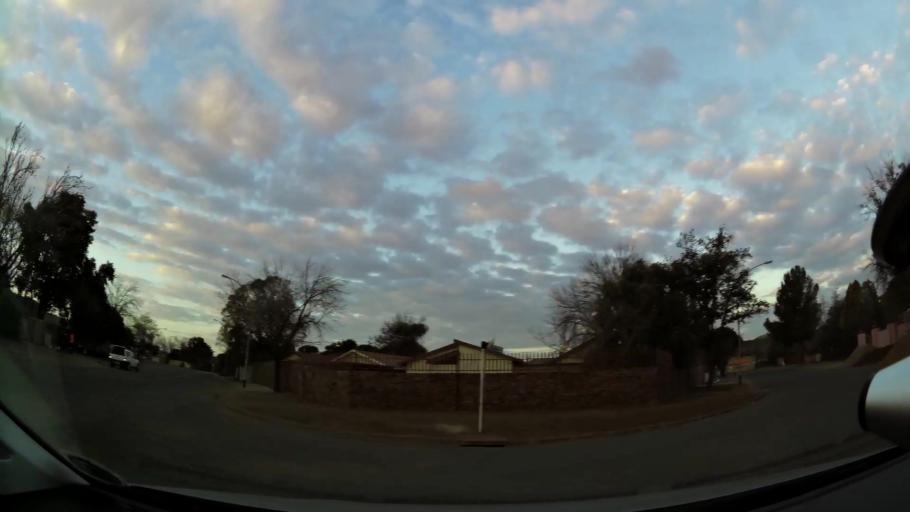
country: ZA
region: Orange Free State
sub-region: Mangaung Metropolitan Municipality
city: Bloemfontein
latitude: -29.1735
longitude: 26.1908
